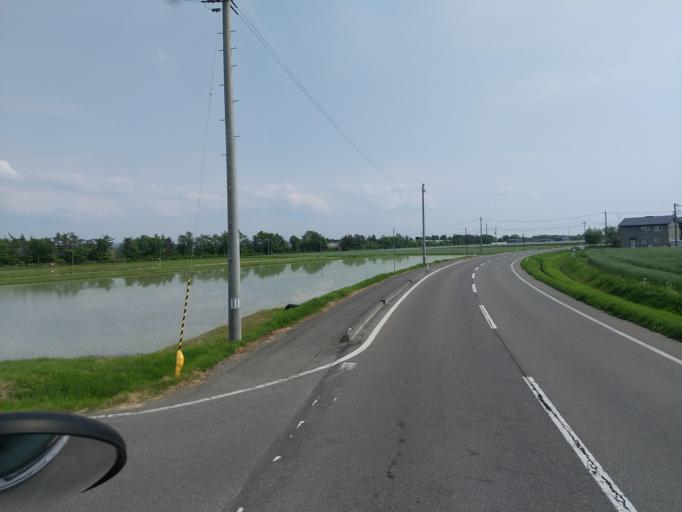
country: JP
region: Iwate
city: Hanamaki
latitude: 39.3963
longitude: 141.0900
